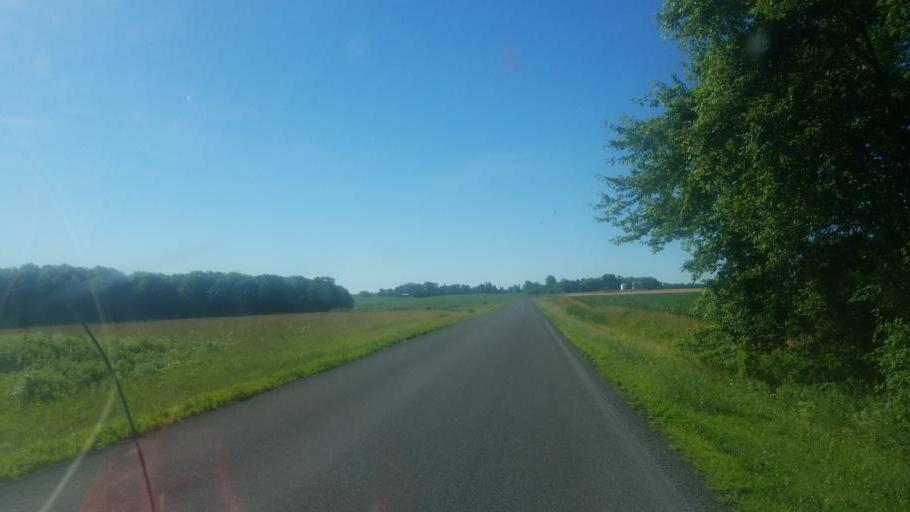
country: US
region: New York
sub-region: Ontario County
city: Phelps
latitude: 42.8947
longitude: -77.0522
